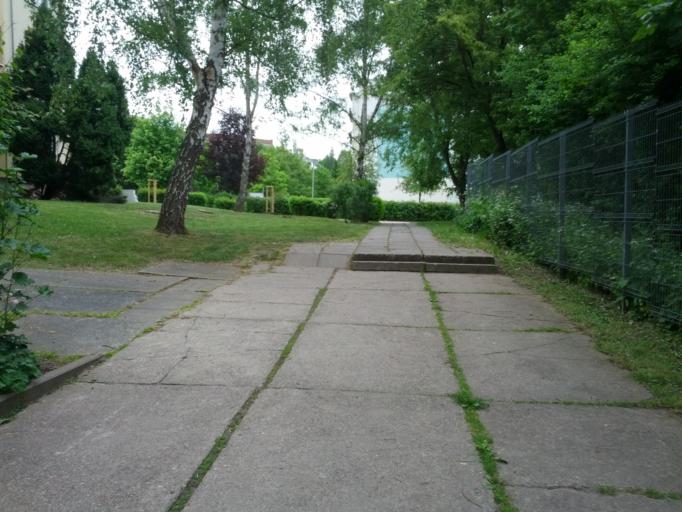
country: DE
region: Thuringia
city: Eisenach
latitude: 50.9947
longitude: 10.3058
